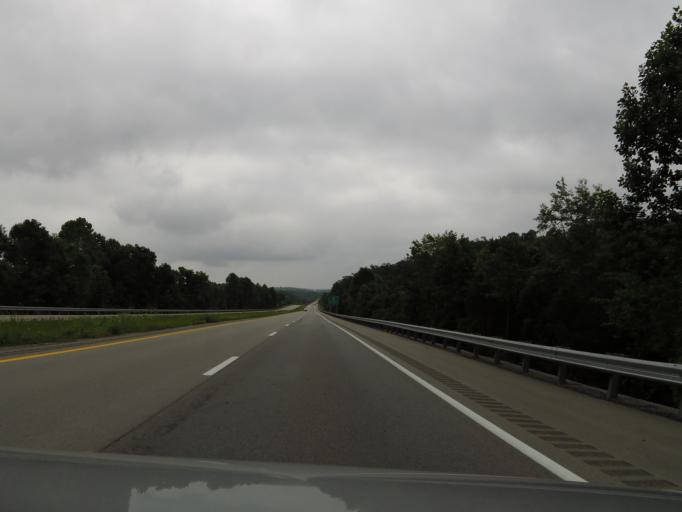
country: US
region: Kentucky
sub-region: Ohio County
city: Oak Grove
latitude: 37.4112
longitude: -86.5281
